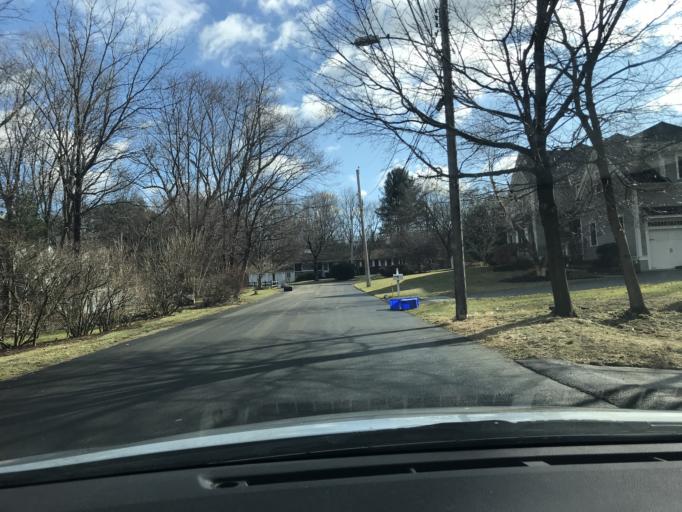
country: US
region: Massachusetts
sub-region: Middlesex County
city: Lexington
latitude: 42.4732
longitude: -71.2238
